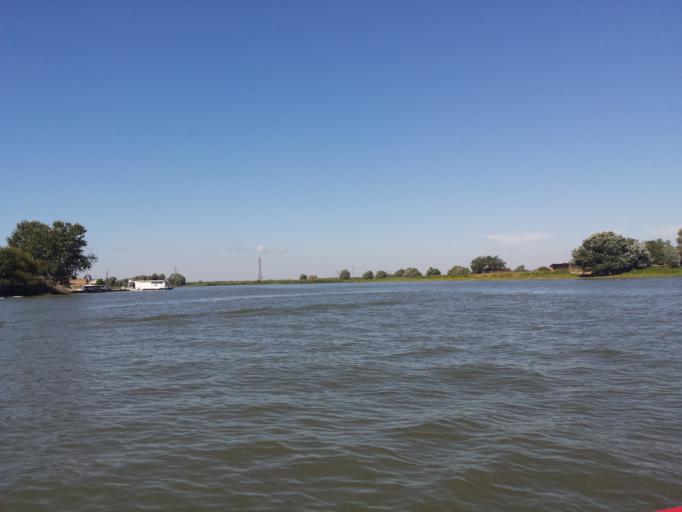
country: RO
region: Tulcea
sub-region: Comuna Crisan
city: Crisan
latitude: 45.2295
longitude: 29.2481
